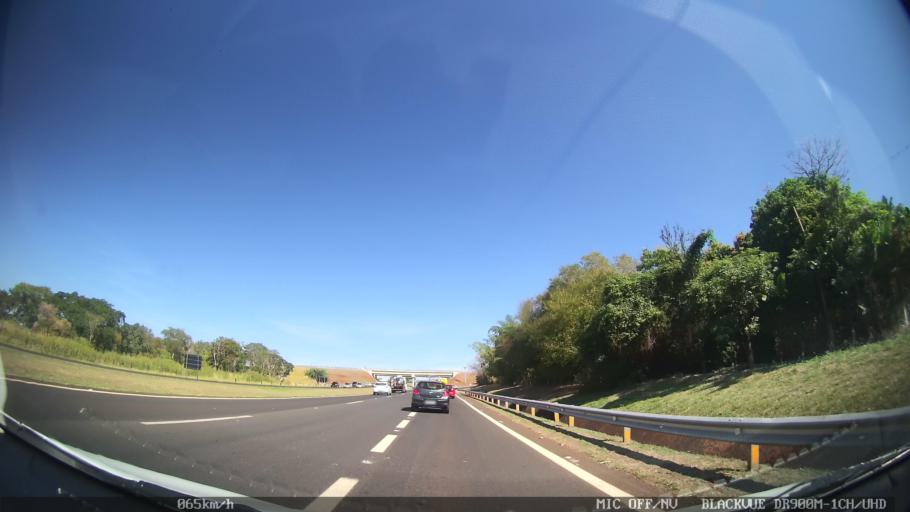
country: BR
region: Sao Paulo
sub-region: Ribeirao Preto
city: Ribeirao Preto
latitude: -21.2203
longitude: -47.7755
